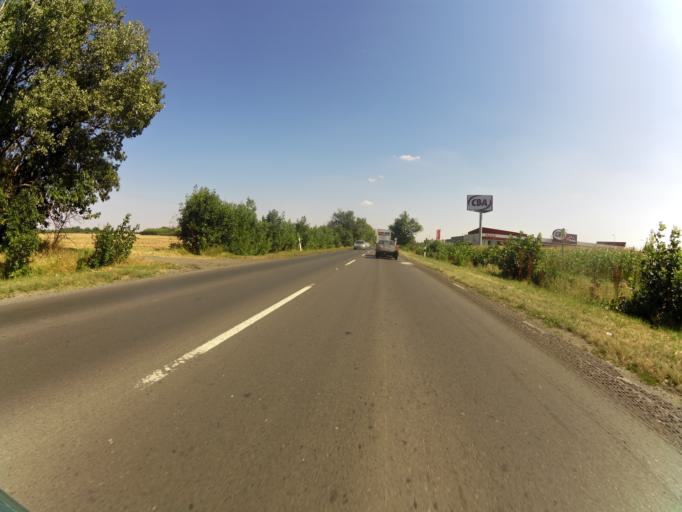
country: HU
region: Csongrad
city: Szeged
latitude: 46.2885
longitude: 20.0871
